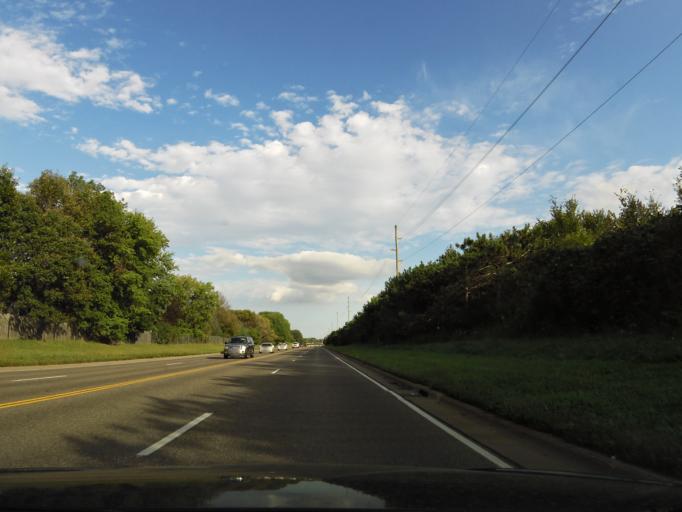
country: US
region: Minnesota
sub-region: Scott County
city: Prior Lake
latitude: 44.6986
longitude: -93.3890
